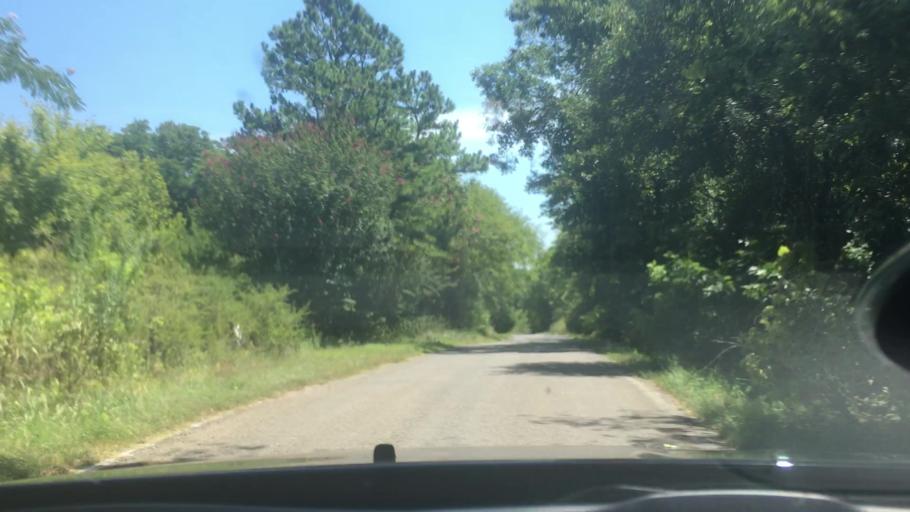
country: US
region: Oklahoma
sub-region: Bryan County
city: Durant
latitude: 33.9828
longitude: -96.2487
